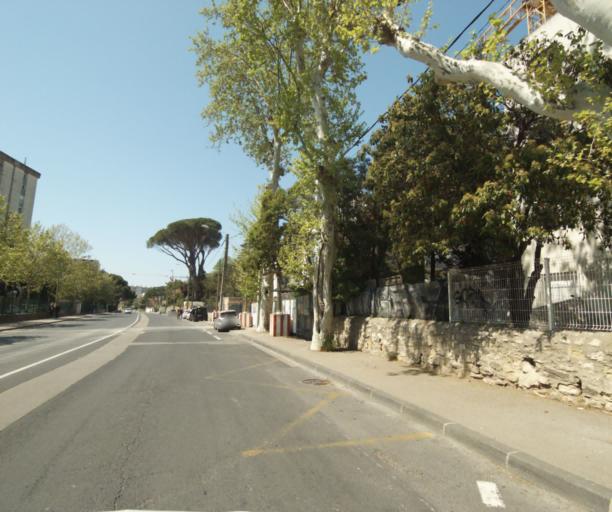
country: FR
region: Languedoc-Roussillon
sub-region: Departement de l'Herault
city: Juvignac
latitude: 43.6140
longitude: 3.8382
